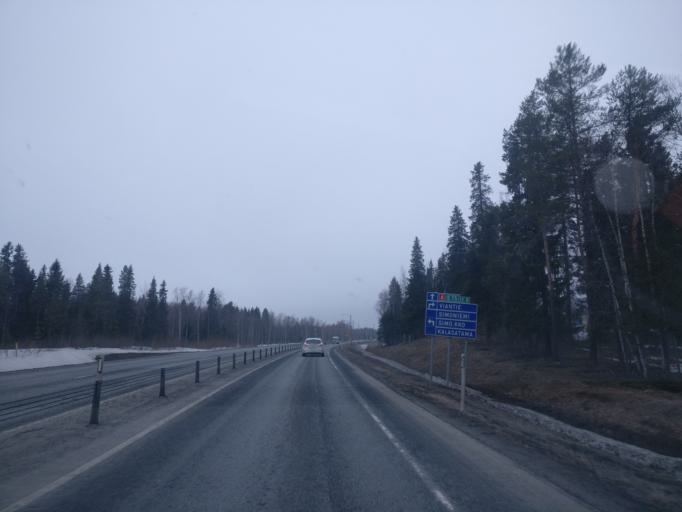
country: FI
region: Lapland
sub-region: Kemi-Tornio
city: Simo
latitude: 65.6687
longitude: 24.9358
